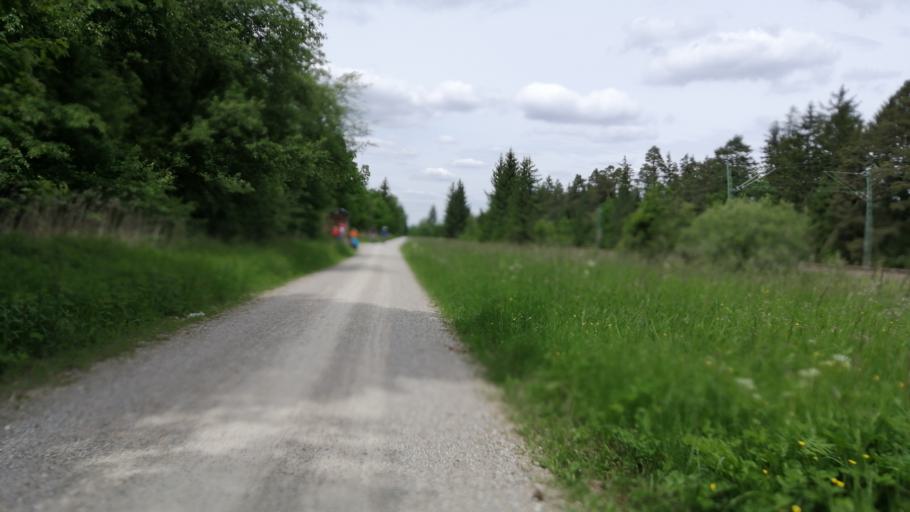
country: DE
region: Bavaria
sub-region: Upper Bavaria
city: Oberhaching
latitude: 48.0545
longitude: 11.5672
